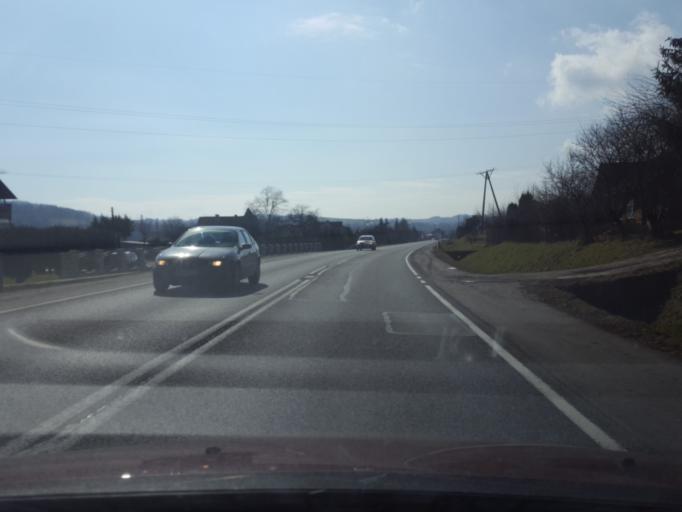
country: PL
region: Lesser Poland Voivodeship
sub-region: Powiat nowosadecki
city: Lososina Dolna
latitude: 49.7620
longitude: 20.6338
